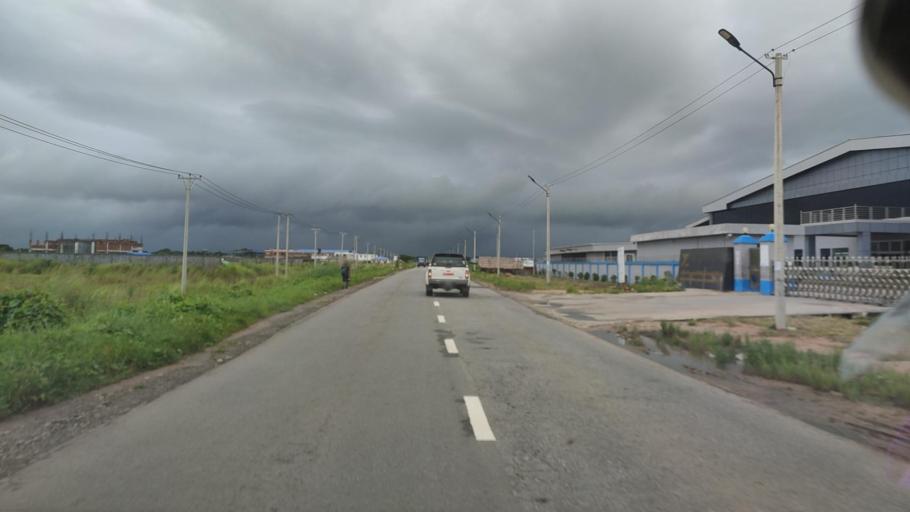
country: MM
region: Bago
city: Bago
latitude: 17.3853
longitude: 96.4971
